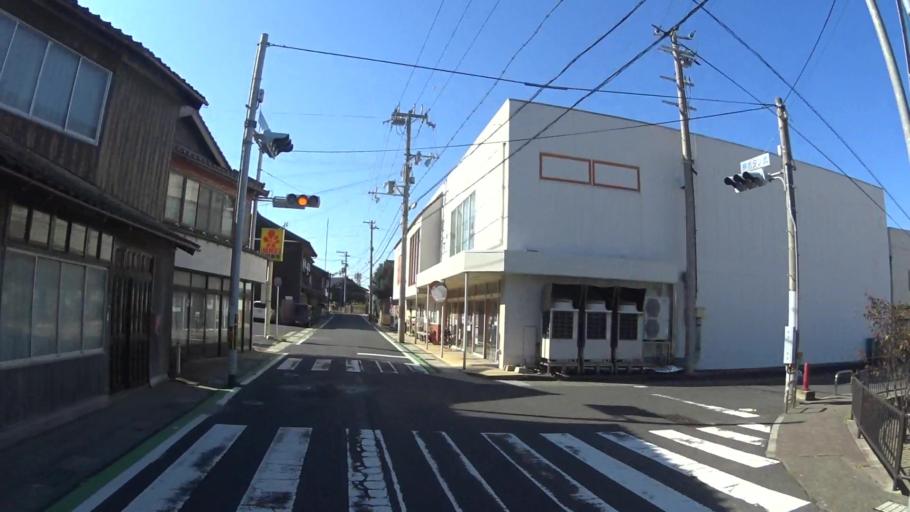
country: JP
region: Kyoto
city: Miyazu
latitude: 35.7377
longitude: 135.0892
